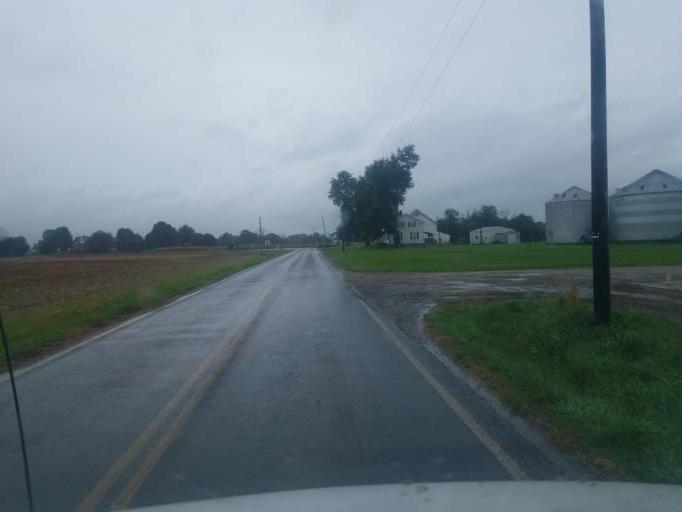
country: US
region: Ohio
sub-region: Medina County
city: Seville
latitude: 40.9908
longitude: -81.8582
